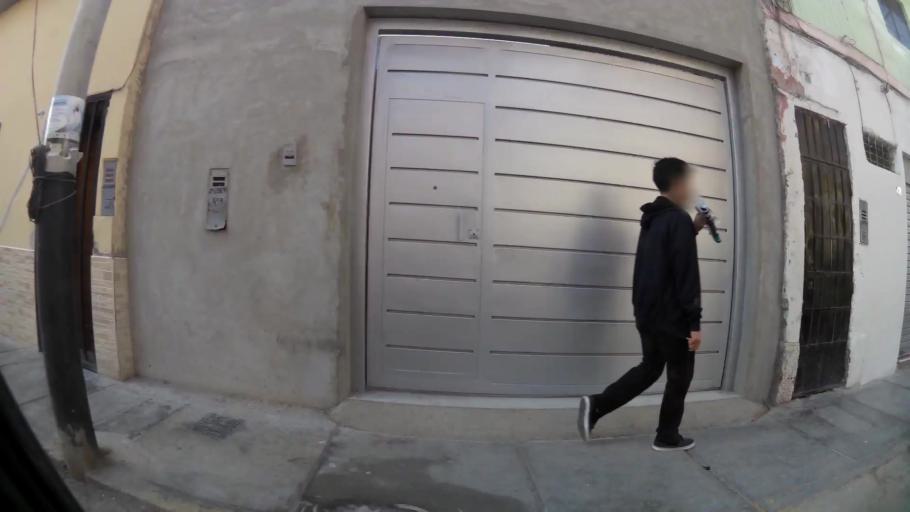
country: PE
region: Lambayeque
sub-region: Provincia de Chiclayo
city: Chiclayo
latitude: -6.7743
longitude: -79.8397
